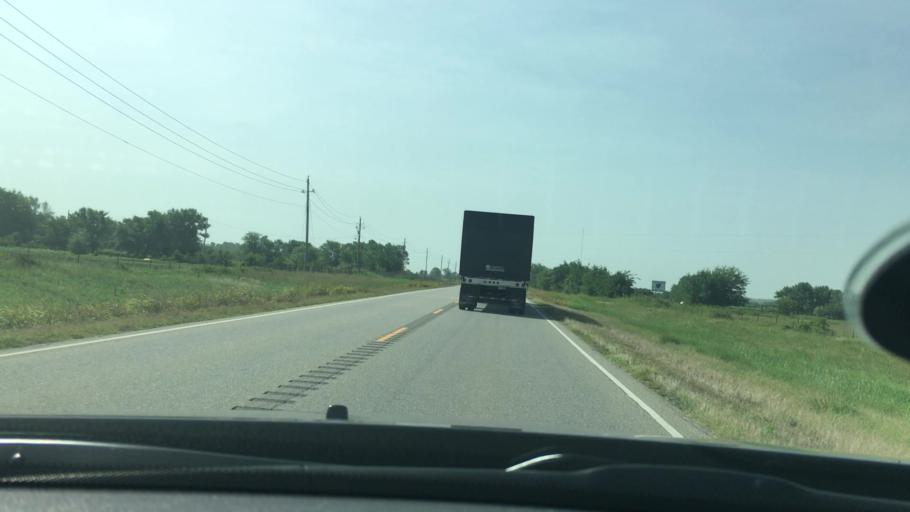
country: US
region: Oklahoma
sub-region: Atoka County
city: Atoka
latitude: 34.4342
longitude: -96.1998
